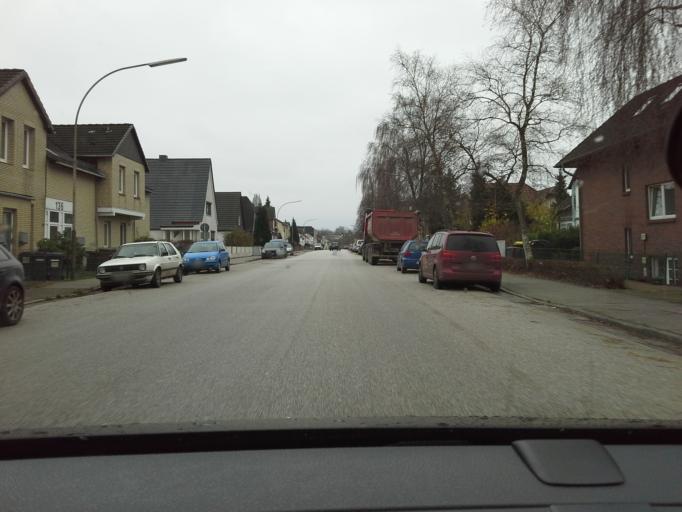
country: DE
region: Schleswig-Holstein
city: Quickborn
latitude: 53.7360
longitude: 9.8925
